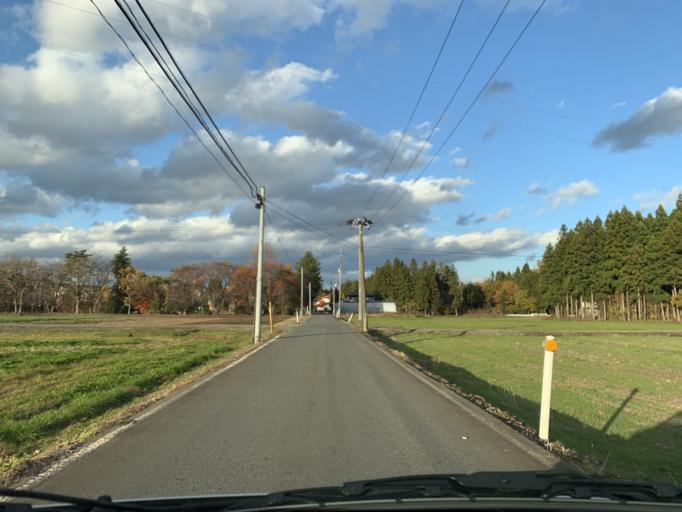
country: JP
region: Iwate
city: Mizusawa
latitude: 39.1257
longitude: 141.0301
